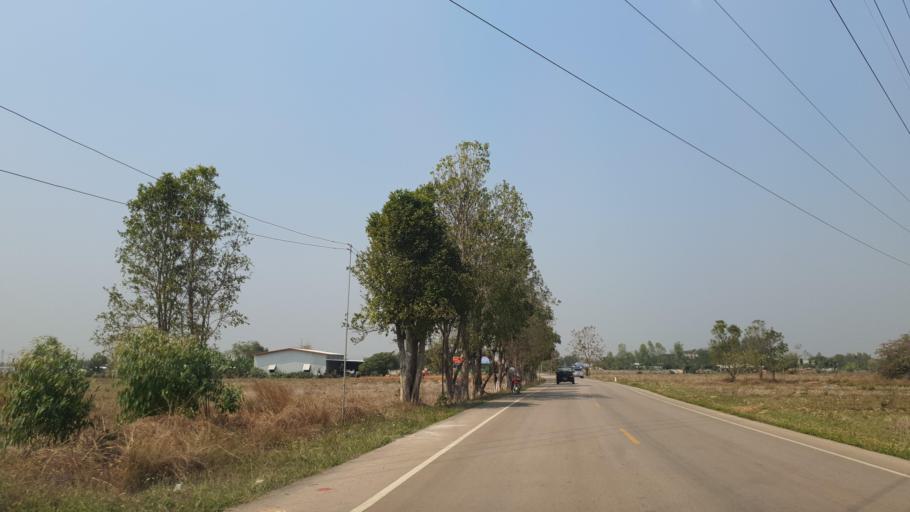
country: TH
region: Lamphun
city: Lamphun
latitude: 18.5506
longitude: 99.0803
